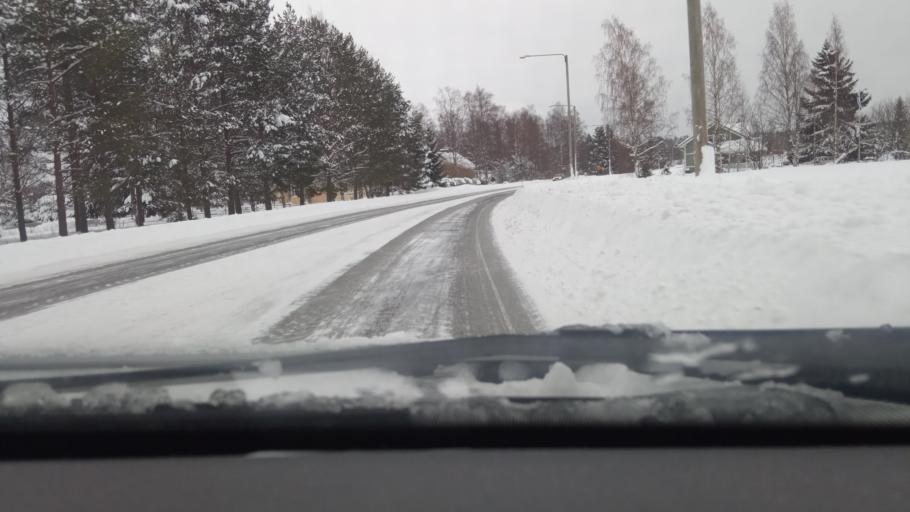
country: FI
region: Southern Ostrobothnia
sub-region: Jaerviseutu
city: Alajaervi
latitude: 62.9931
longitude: 23.8331
